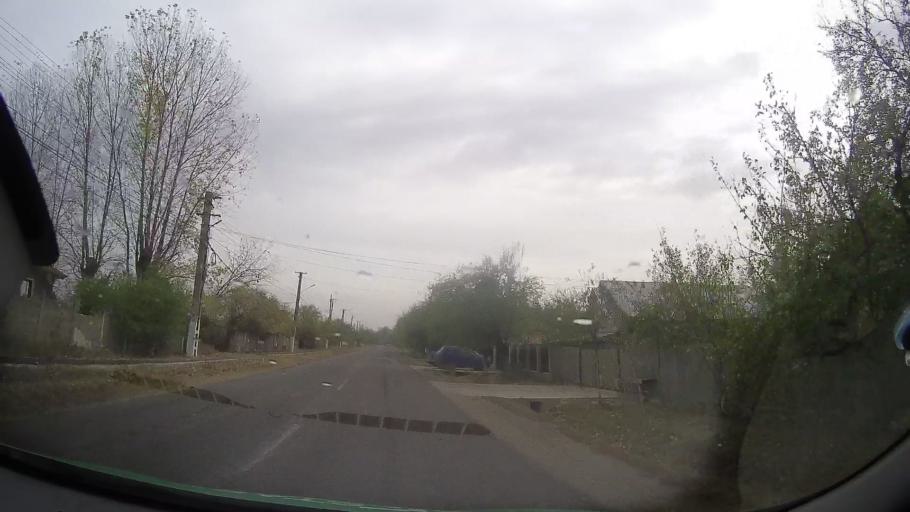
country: RO
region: Prahova
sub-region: Comuna Dumbrava
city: Dumbrava
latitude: 44.8652
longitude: 26.2022
